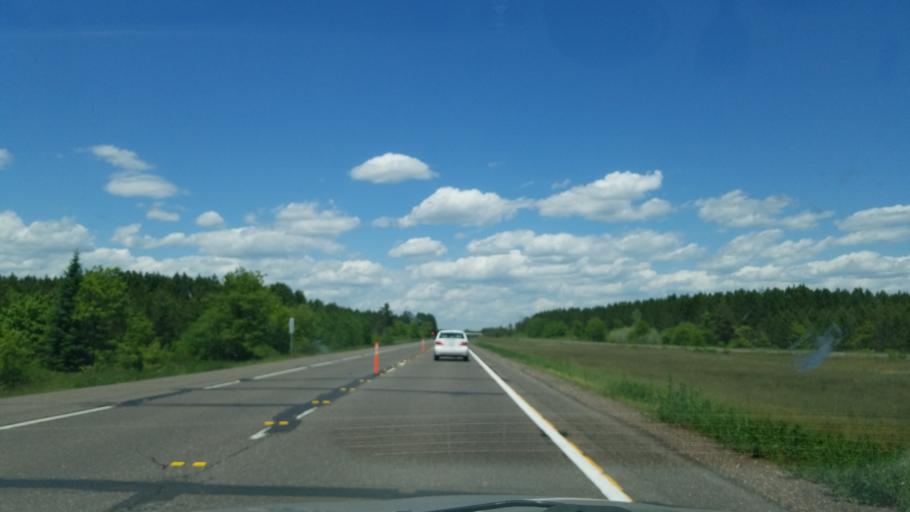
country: US
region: Minnesota
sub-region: Carlton County
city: Moose Lake
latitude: 46.3377
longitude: -92.8172
